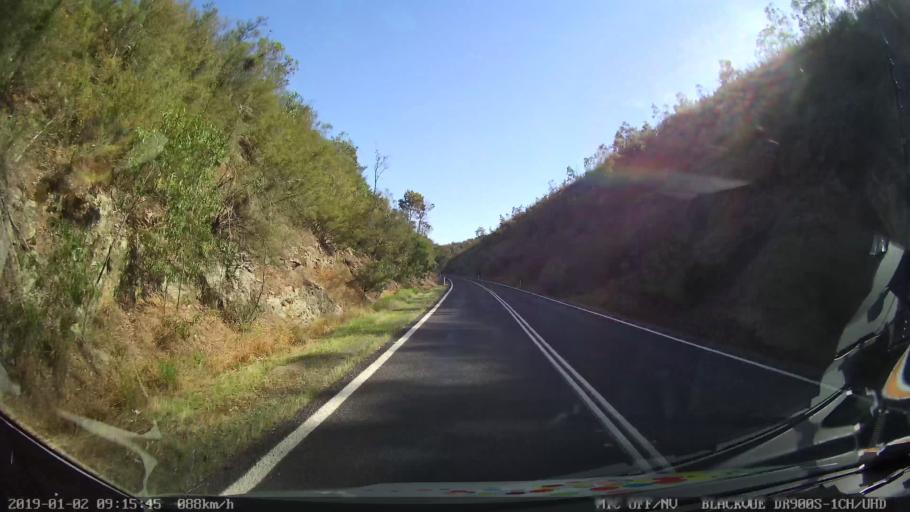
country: AU
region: New South Wales
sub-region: Tumut Shire
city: Tumut
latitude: -35.4615
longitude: 148.2816
